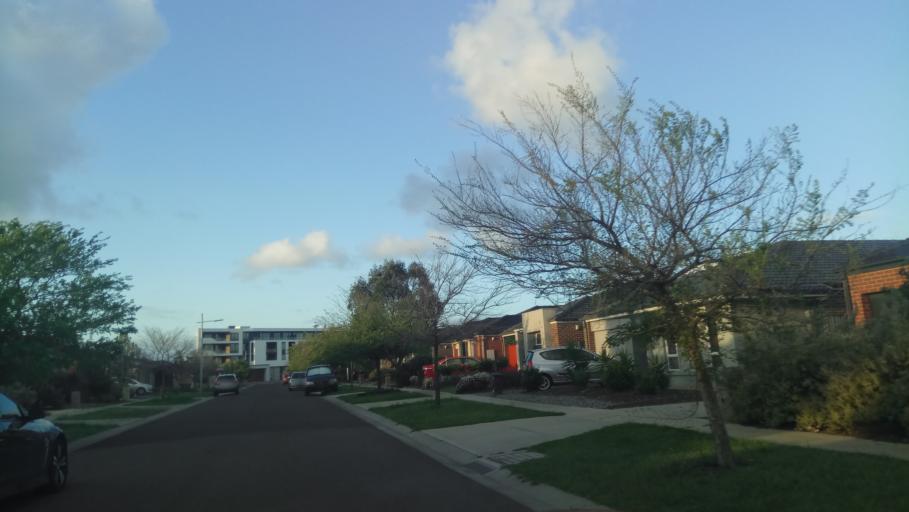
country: AU
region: Victoria
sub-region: Wyndham
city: Point Cook
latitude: -37.9135
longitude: 144.7712
